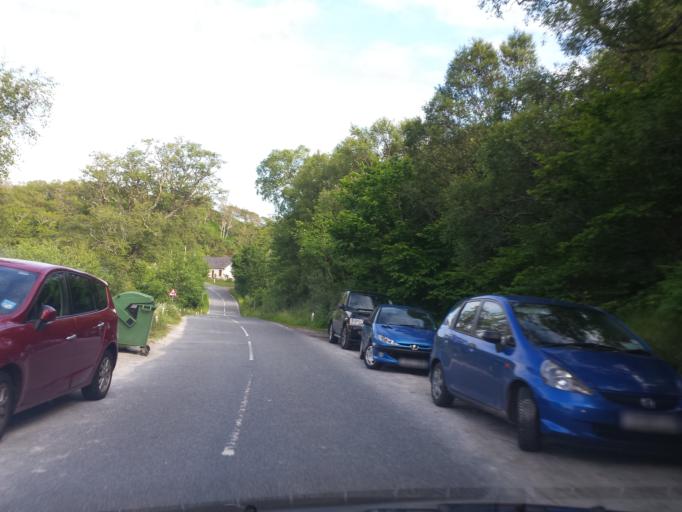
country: GB
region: Scotland
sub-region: Argyll and Bute
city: Isle Of Mull
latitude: 56.9609
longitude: -5.8234
